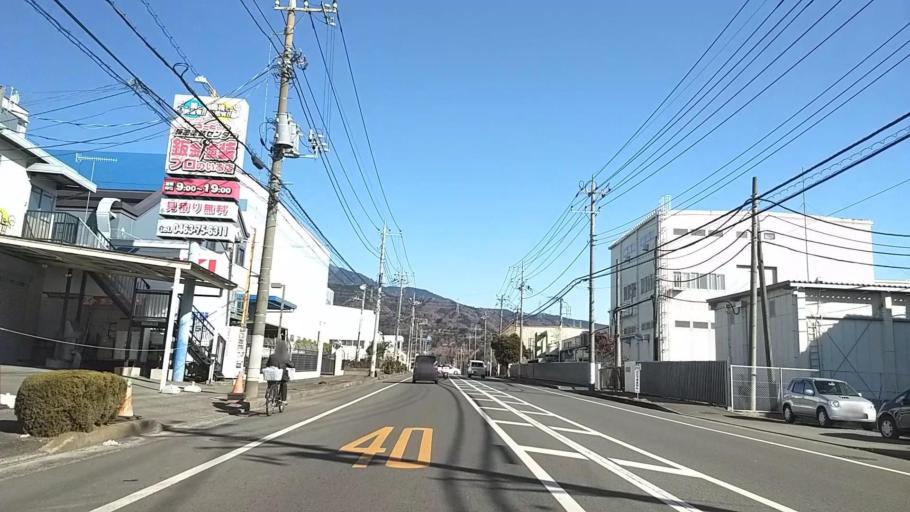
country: JP
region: Kanagawa
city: Hadano
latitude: 35.3866
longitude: 139.2018
